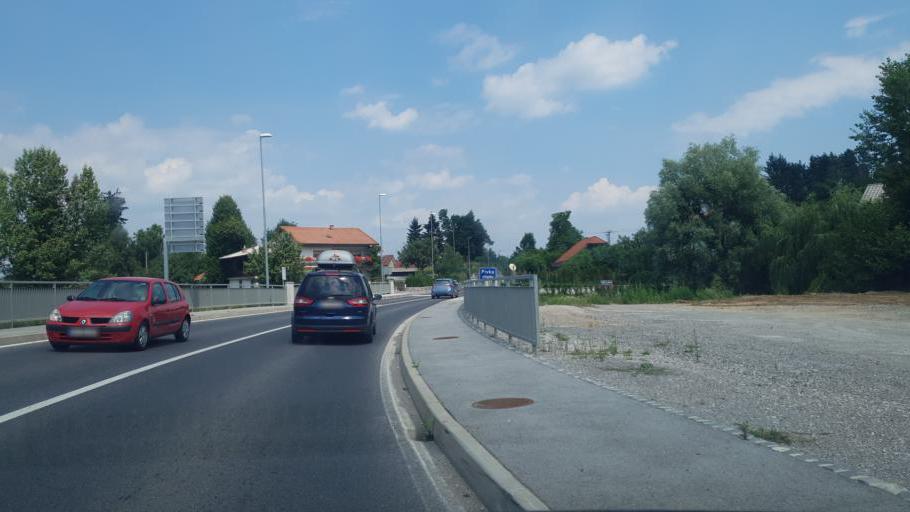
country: SI
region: Pivka
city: Pivka
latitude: 45.7308
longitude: 14.1862
